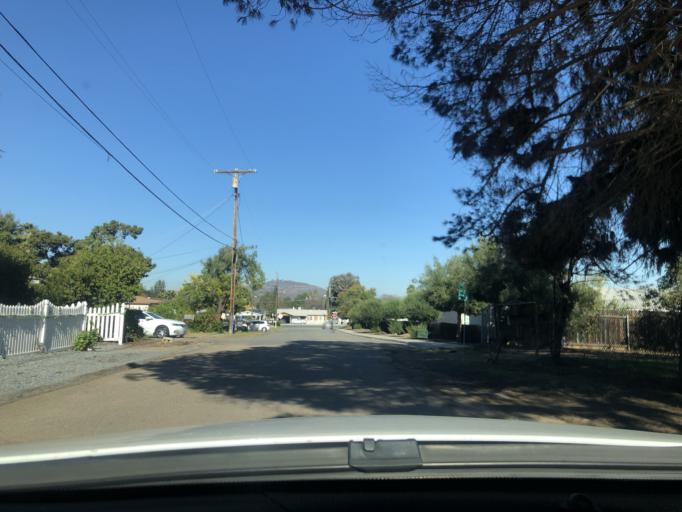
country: US
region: California
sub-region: San Diego County
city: Bostonia
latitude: 32.7864
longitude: -116.9395
